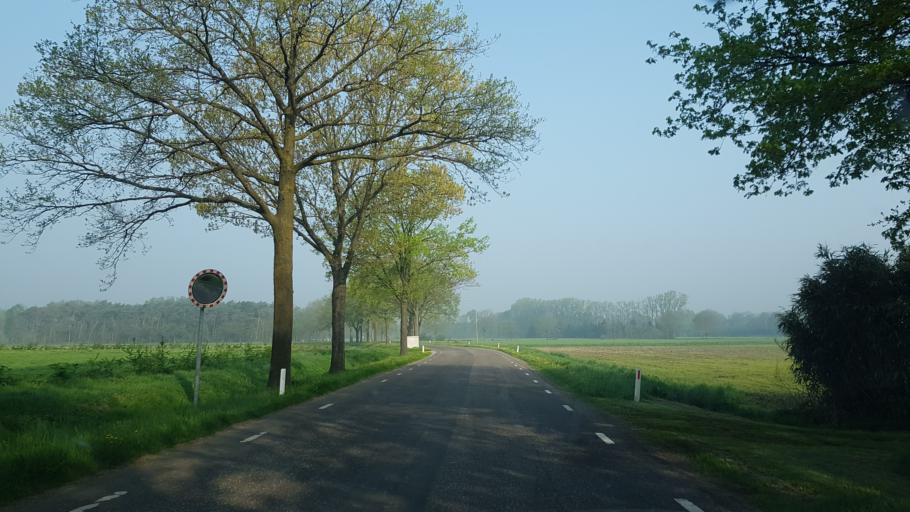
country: NL
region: Limburg
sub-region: Gemeente Nederweert
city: Nederweert
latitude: 51.3121
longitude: 5.7128
